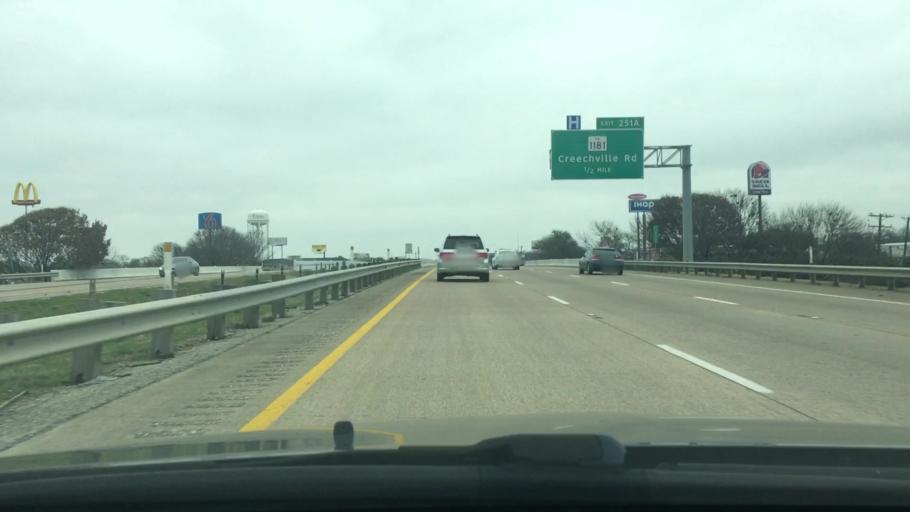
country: US
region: Texas
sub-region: Ellis County
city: Ennis
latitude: 32.3351
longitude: -96.6163
